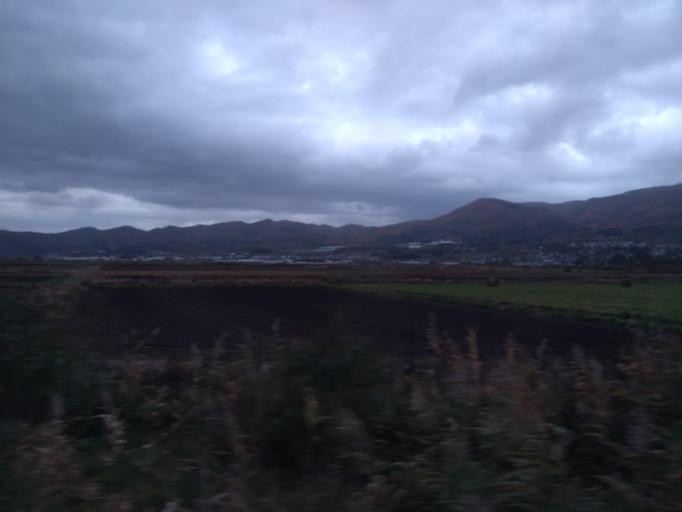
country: JP
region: Hokkaido
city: Nanae
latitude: 41.9006
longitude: 140.6722
